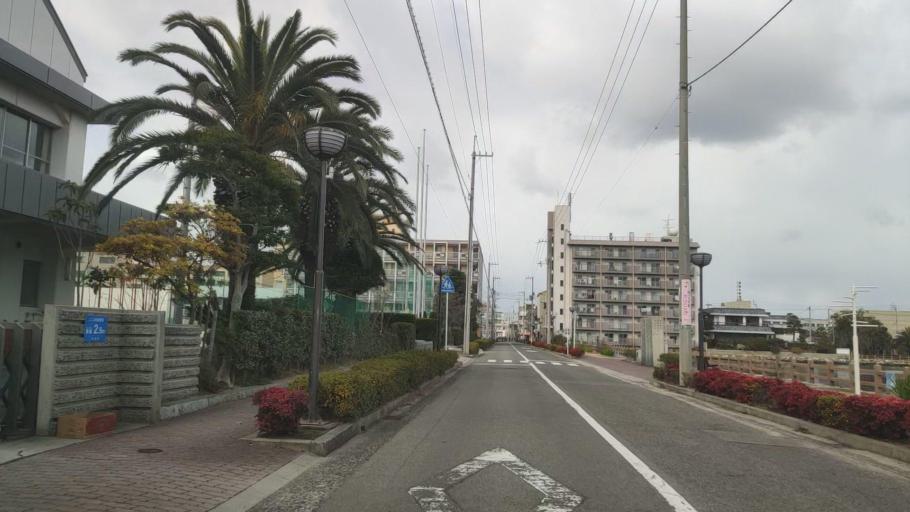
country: JP
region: Ehime
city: Saijo
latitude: 34.0621
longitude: 133.0059
